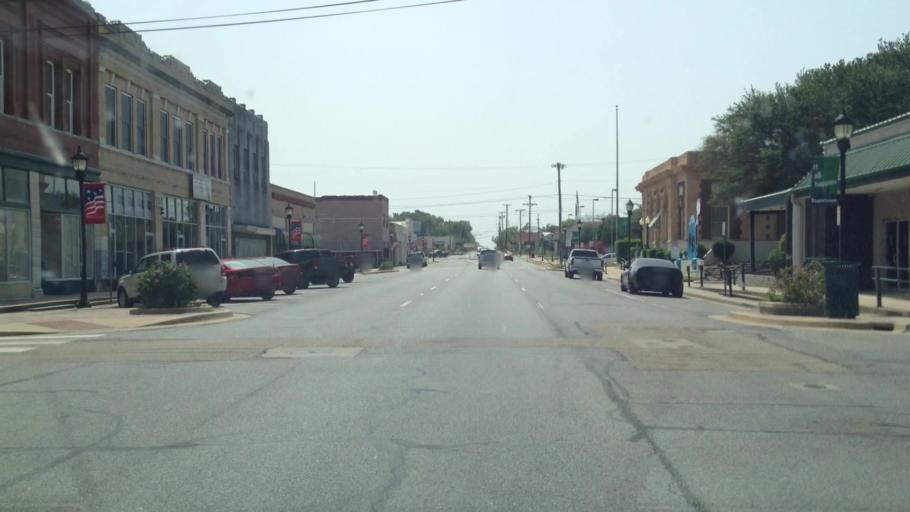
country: US
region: Texas
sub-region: Hunt County
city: Greenville
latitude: 33.1399
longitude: -96.1100
